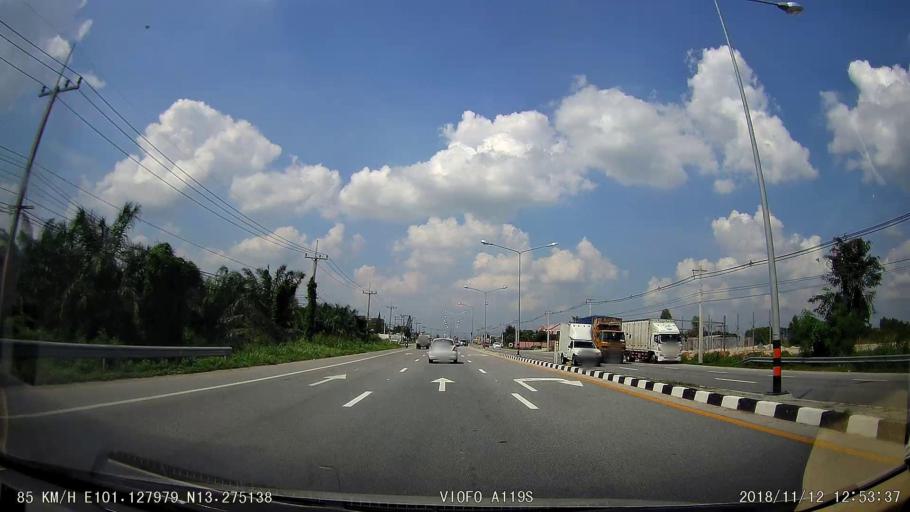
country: TH
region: Chon Buri
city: Ban Bueng
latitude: 13.2754
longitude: 101.1278
